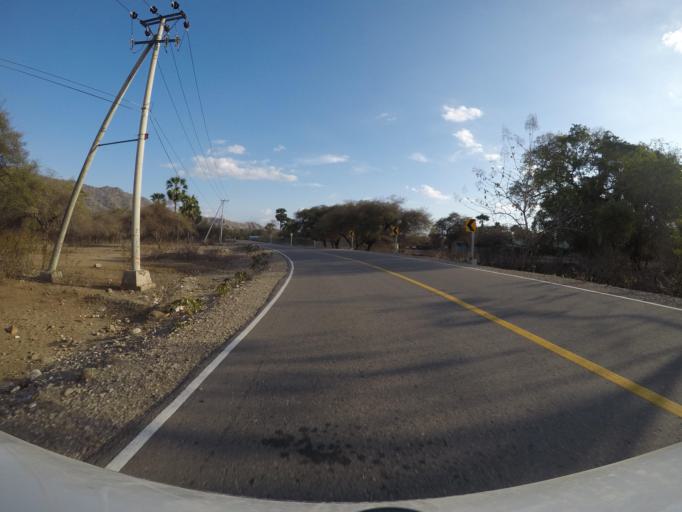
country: ID
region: East Nusa Tenggara
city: Atambua
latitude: -8.9132
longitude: 124.9940
